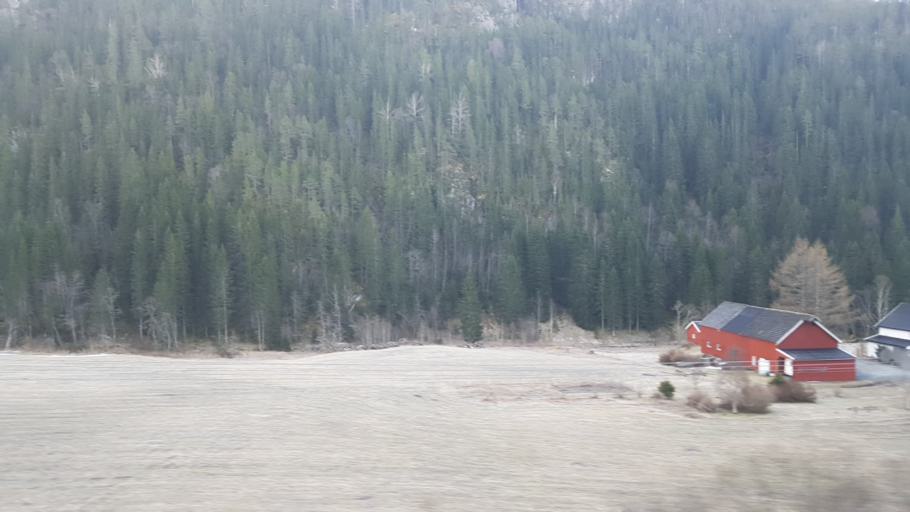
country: NO
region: Nord-Trondelag
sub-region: Stjordal
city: Stjordalshalsen
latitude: 63.5994
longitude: 11.0240
